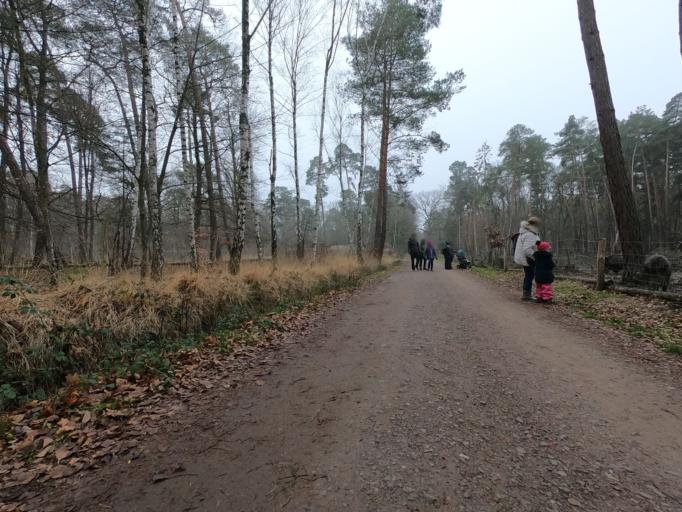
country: DE
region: Hesse
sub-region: Regierungsbezirk Darmstadt
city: Hanau am Main
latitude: 50.0830
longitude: 8.9039
